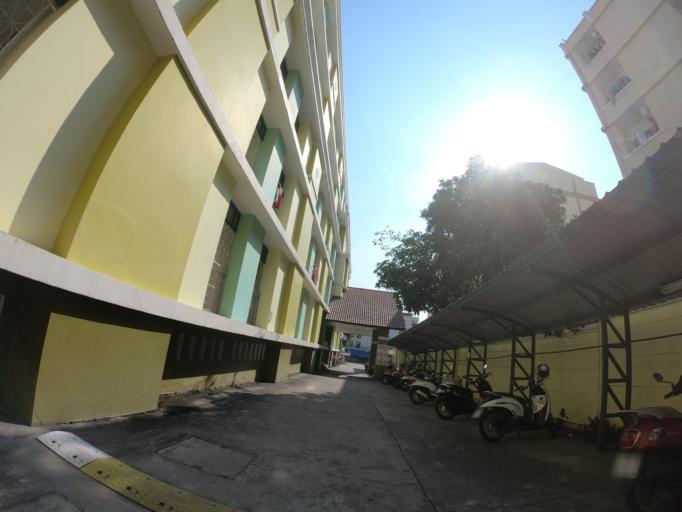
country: TH
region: Chiang Mai
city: Chiang Mai
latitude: 18.7907
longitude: 98.9582
